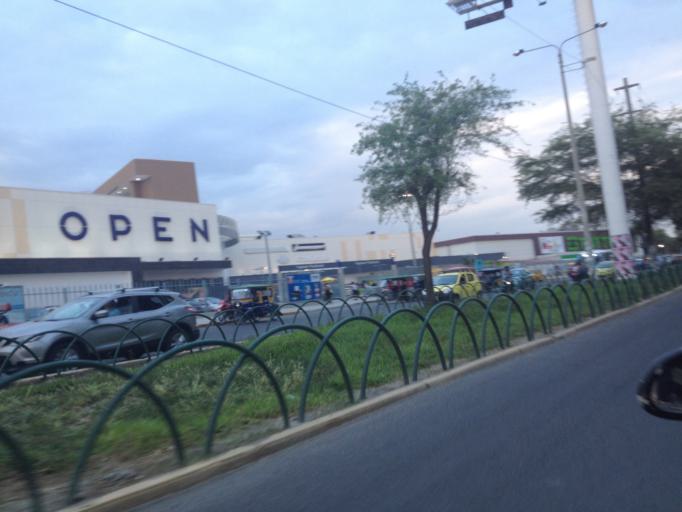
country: PE
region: Piura
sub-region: Provincia de Piura
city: Piura
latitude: -5.1830
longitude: -80.6229
